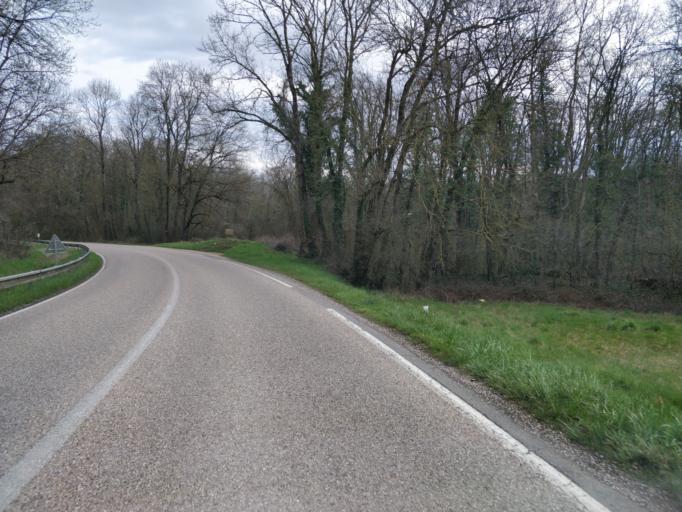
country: FR
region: Lorraine
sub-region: Departement de la Moselle
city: Gandrange
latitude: 49.2833
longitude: 6.1274
